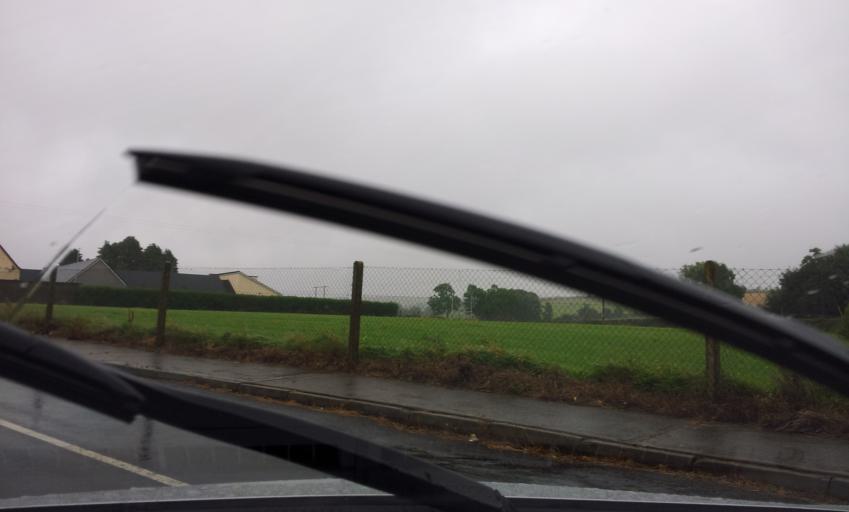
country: IE
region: Leinster
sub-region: Kilkenny
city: Thomastown
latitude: 52.4092
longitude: -7.0750
